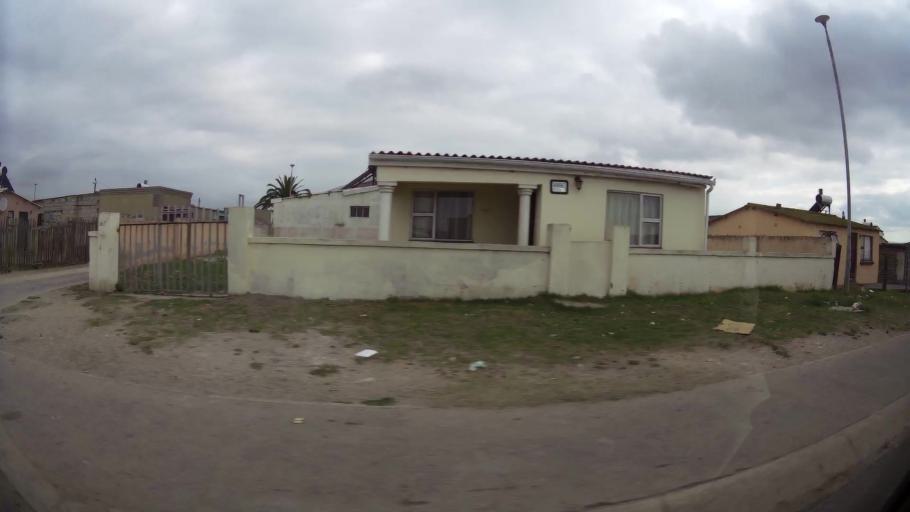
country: ZA
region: Eastern Cape
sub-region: Nelson Mandela Bay Metropolitan Municipality
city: Port Elizabeth
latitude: -33.8762
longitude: 25.5964
